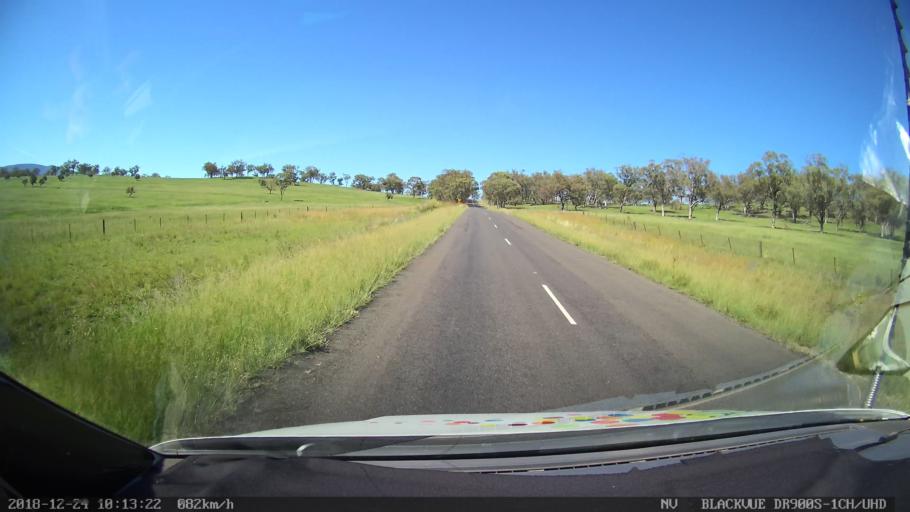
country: AU
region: New South Wales
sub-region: Liverpool Plains
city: Quirindi
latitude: -31.6890
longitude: 150.6402
